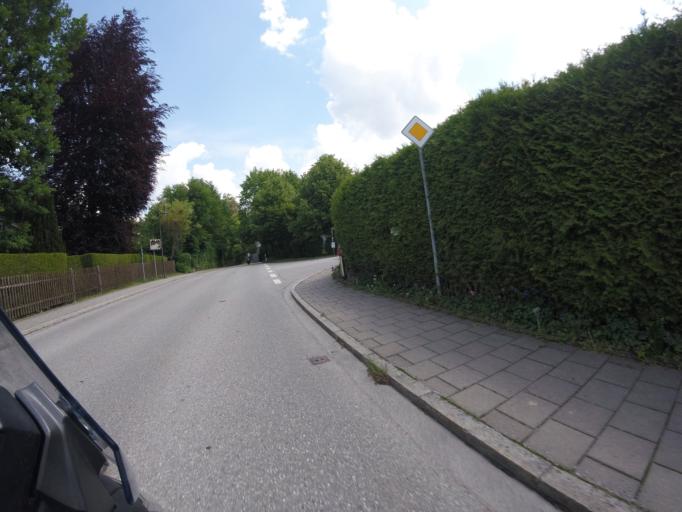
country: DE
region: Bavaria
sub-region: Upper Bavaria
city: Schaftlarn
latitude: 47.9886
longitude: 11.4628
